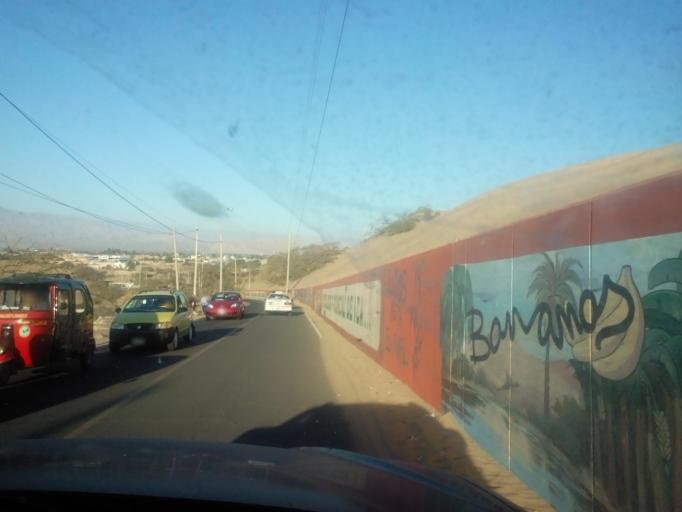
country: PE
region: Ica
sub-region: Provincia de Ica
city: Ica
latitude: -14.0867
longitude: -75.7598
